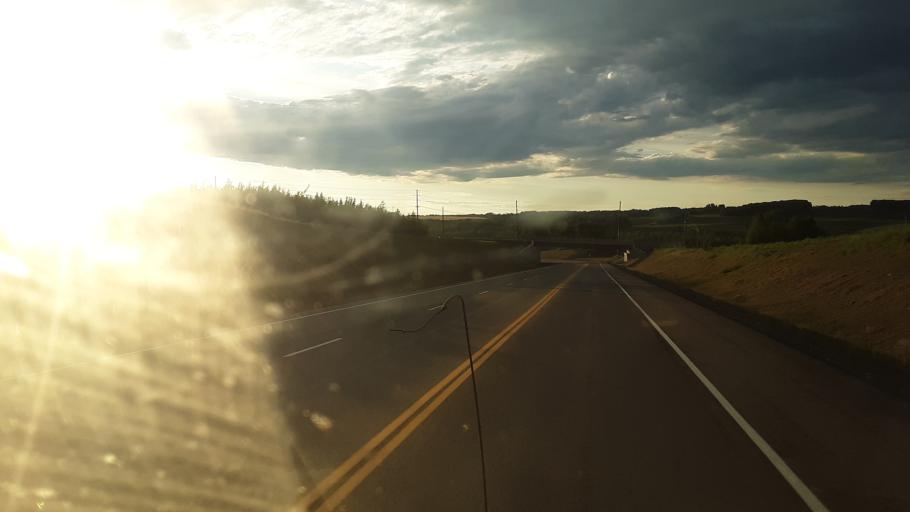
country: US
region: Maine
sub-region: Aroostook County
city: Presque Isle
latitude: 46.6889
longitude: -67.9771
